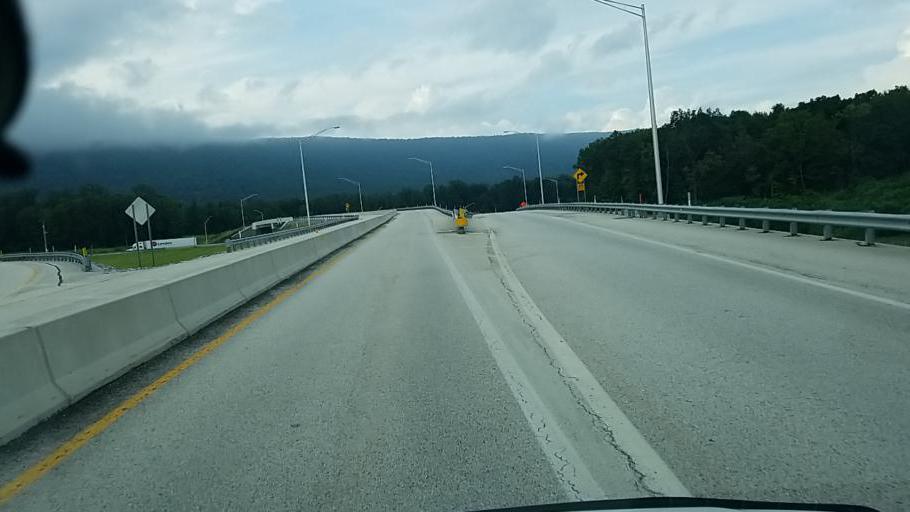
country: US
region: Pennsylvania
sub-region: Franklin County
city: Doylestown
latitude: 40.1561
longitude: -77.6137
